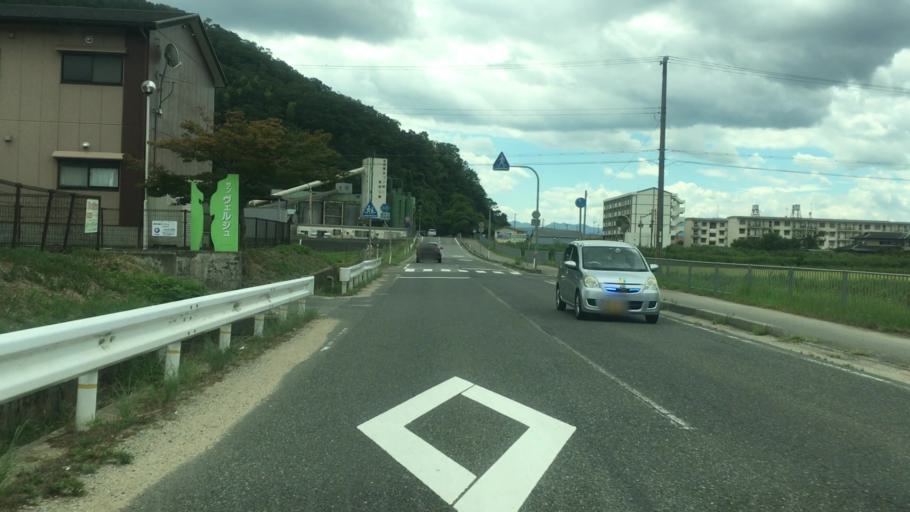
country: JP
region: Hyogo
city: Toyooka
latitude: 35.5501
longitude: 134.8424
